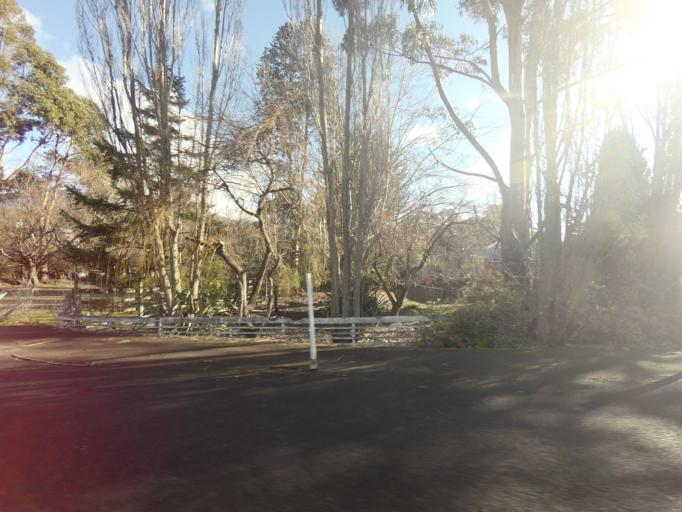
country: AU
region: Tasmania
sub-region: Glenorchy
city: Berriedale
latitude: -42.8388
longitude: 147.1980
